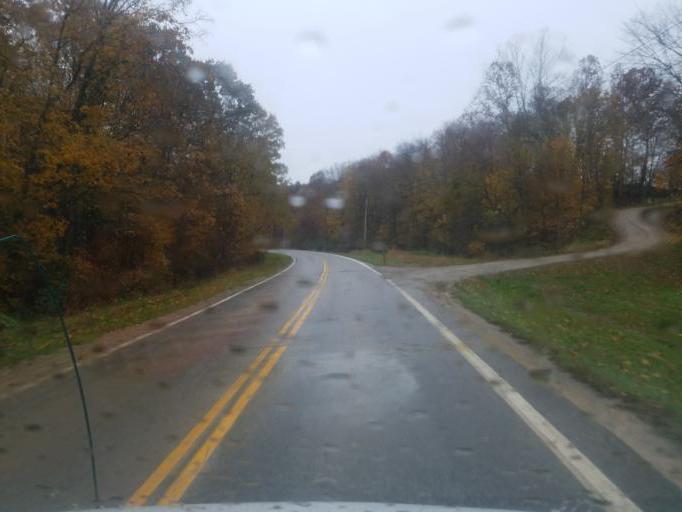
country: US
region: Ohio
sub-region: Washington County
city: Beverly
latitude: 39.4658
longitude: -81.6415
